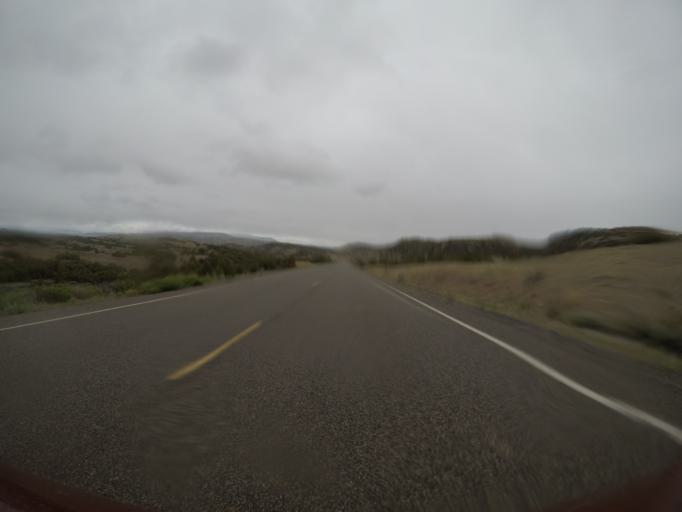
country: US
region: Wyoming
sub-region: Big Horn County
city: Lovell
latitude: 45.0200
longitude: -108.2693
